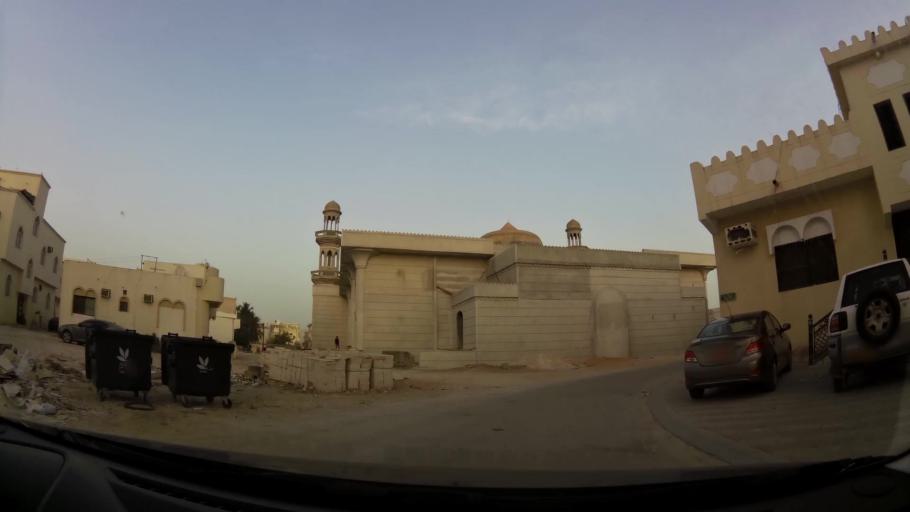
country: OM
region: Zufar
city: Salalah
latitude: 17.0196
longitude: 54.1243
